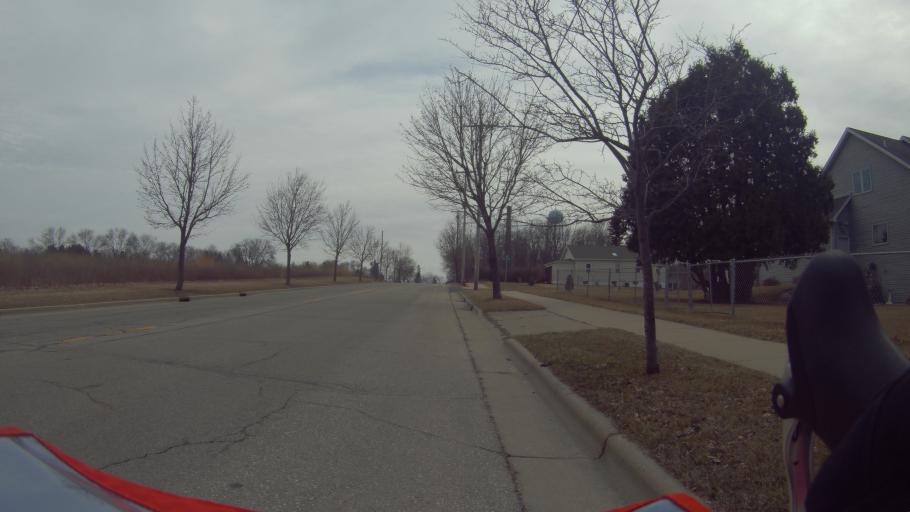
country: US
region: Wisconsin
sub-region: Dane County
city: Maple Bluff
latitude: 43.1372
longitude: -89.3978
